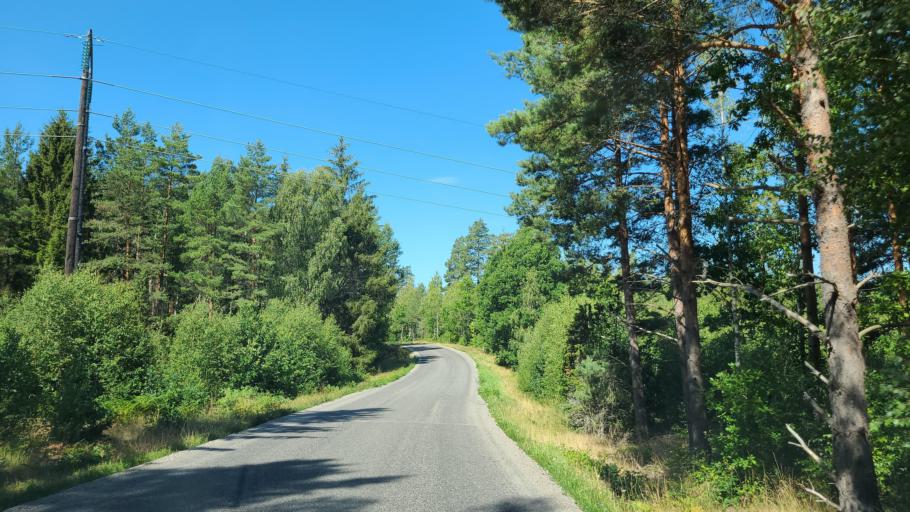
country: SE
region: Kalmar
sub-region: Kalmar Kommun
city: Ljungbyholm
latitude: 56.5685
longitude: 16.0565
